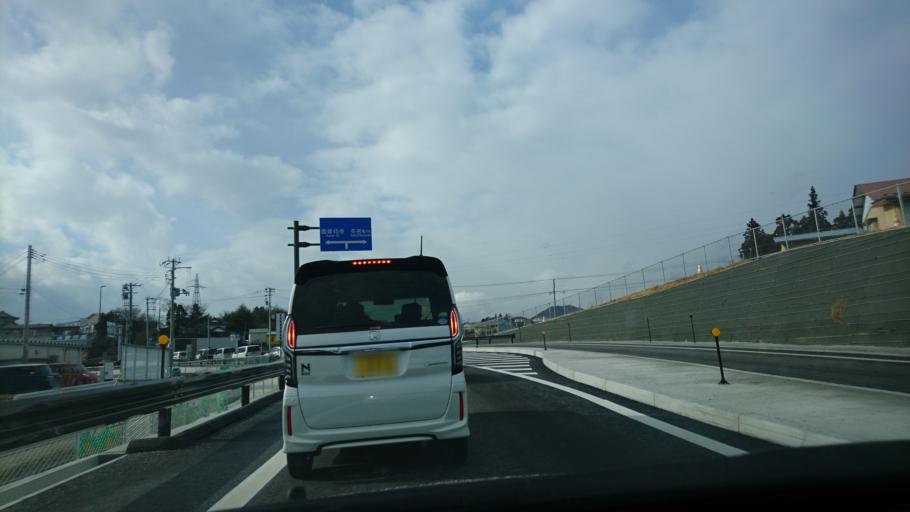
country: JP
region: Iwate
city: Ofunato
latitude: 38.7920
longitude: 141.5182
